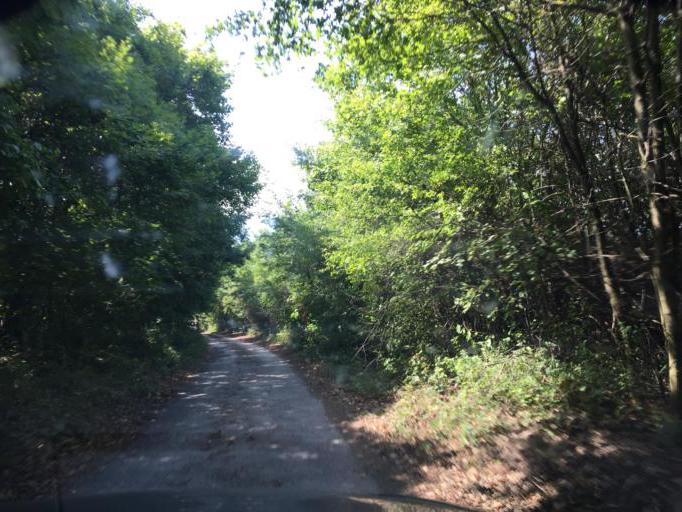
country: HU
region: Pest
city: Veroce
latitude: 47.8312
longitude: 19.0506
